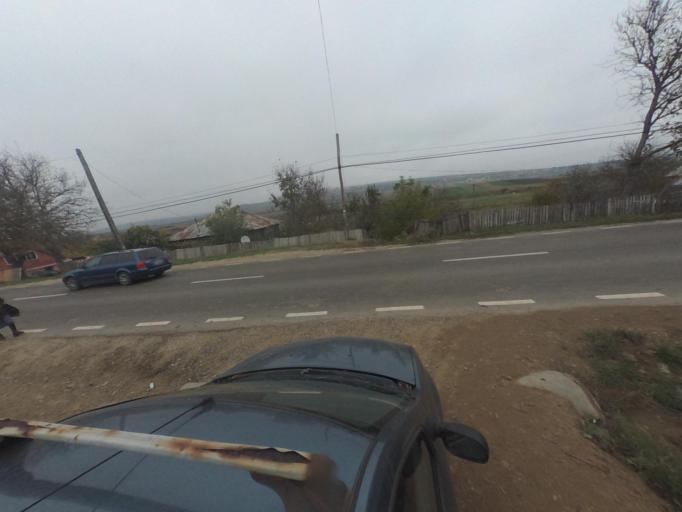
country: RO
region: Vaslui
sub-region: Comuna Bacesti
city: Bacesti
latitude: 46.8334
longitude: 27.2323
